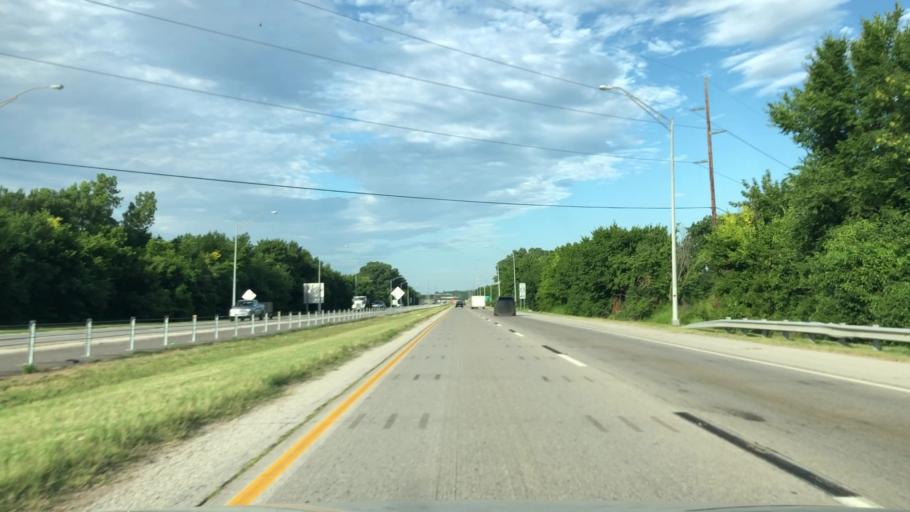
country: US
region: Oklahoma
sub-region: Tulsa County
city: Tulsa
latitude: 36.1845
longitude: -95.9622
